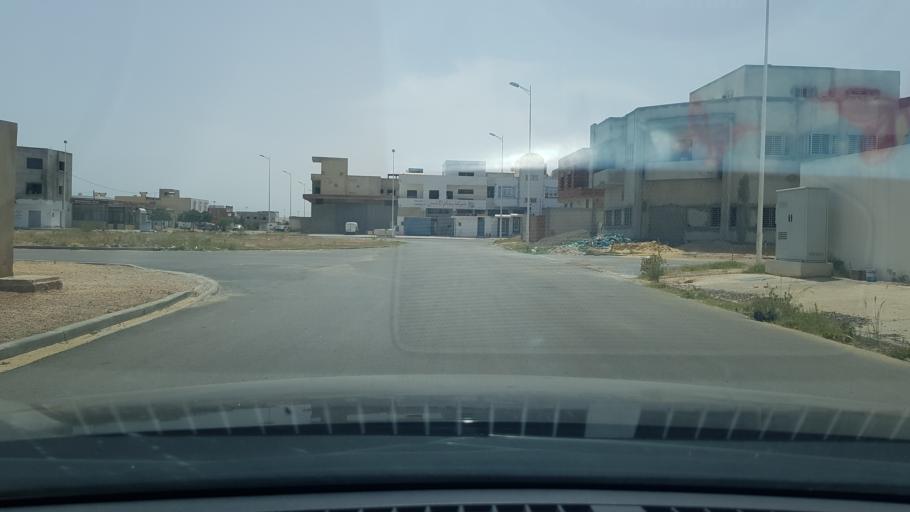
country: TN
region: Safaqis
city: Al Qarmadah
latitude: 34.8266
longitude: 10.7403
